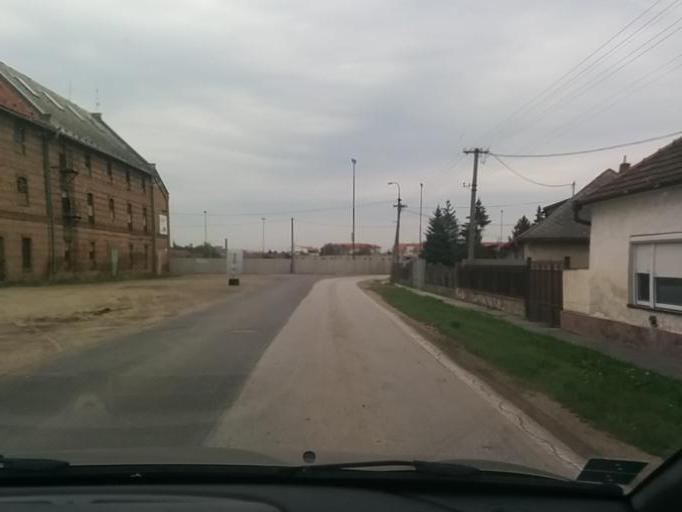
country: SK
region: Trnavsky
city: Sladkovicovo
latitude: 48.2051
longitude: 17.6334
